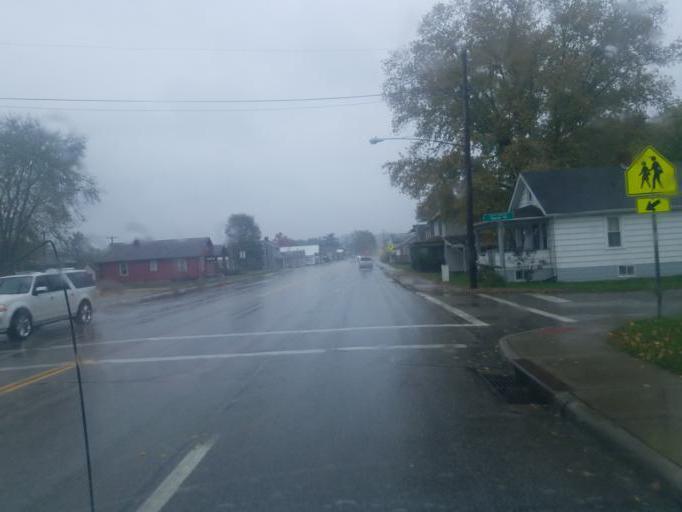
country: US
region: Ohio
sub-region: Muskingum County
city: Pleasant Grove
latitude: 39.8727
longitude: -81.9143
